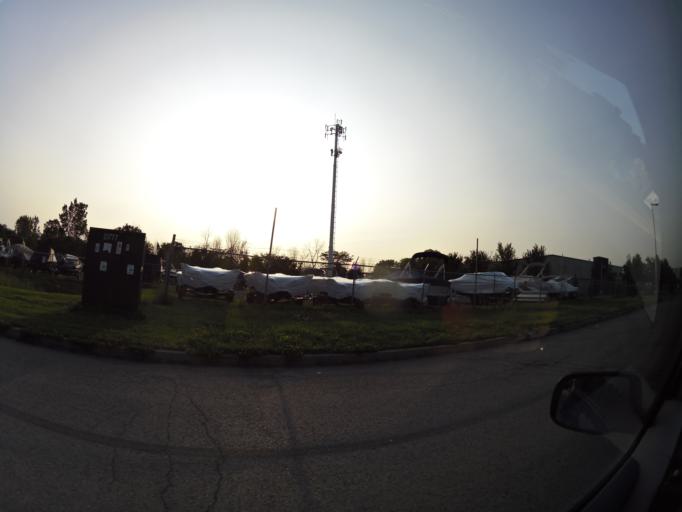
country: CA
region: Ontario
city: Clarence-Rockland
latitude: 45.4895
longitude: -75.4867
